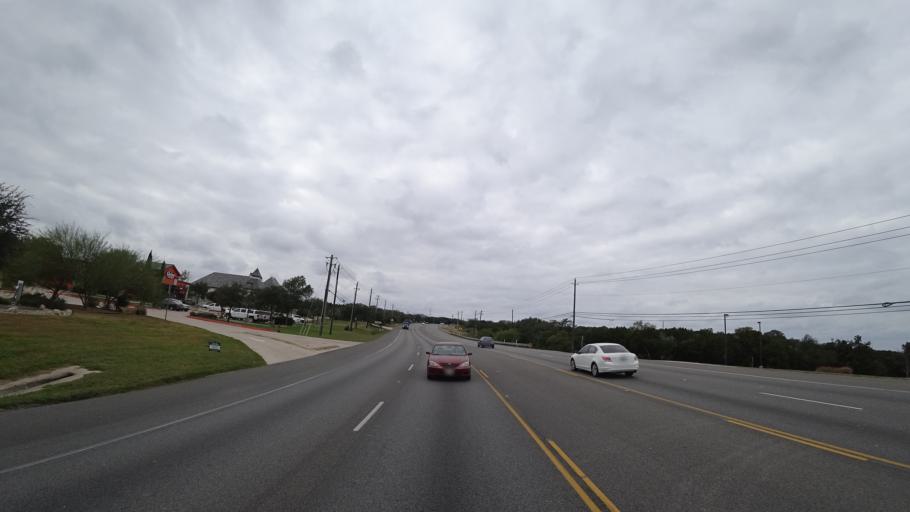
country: US
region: Texas
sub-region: Travis County
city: Bee Cave
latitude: 30.3253
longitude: -97.9590
